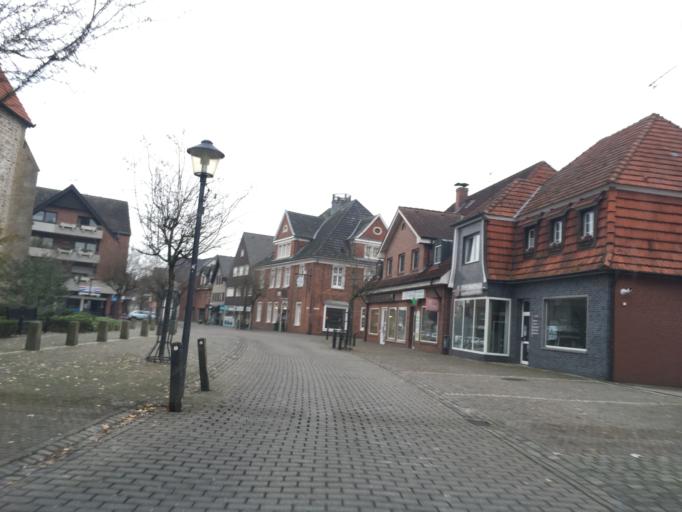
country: DE
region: North Rhine-Westphalia
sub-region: Regierungsbezirk Munster
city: Ostbevern
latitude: 52.0360
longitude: 7.8394
